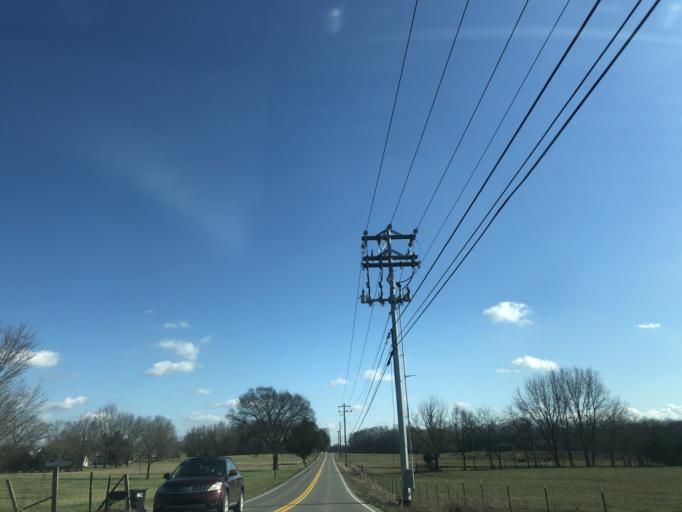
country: US
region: Tennessee
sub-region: Rutherford County
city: Smyrna
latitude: 35.9836
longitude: -86.4149
